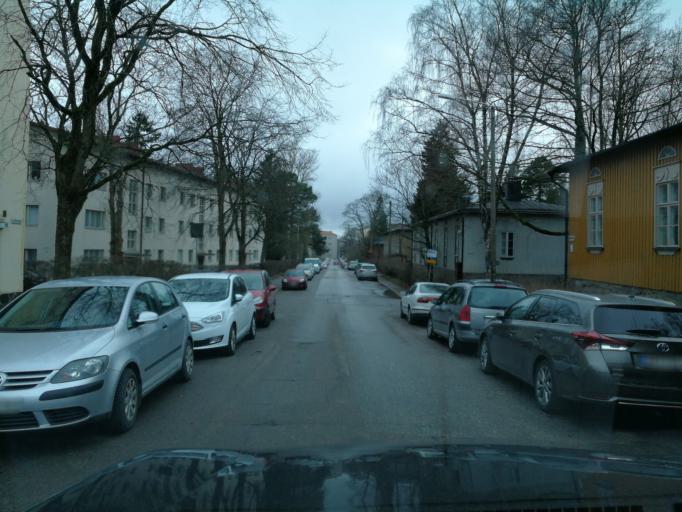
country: FI
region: Uusimaa
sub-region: Helsinki
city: Helsinki
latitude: 60.2124
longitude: 24.9507
